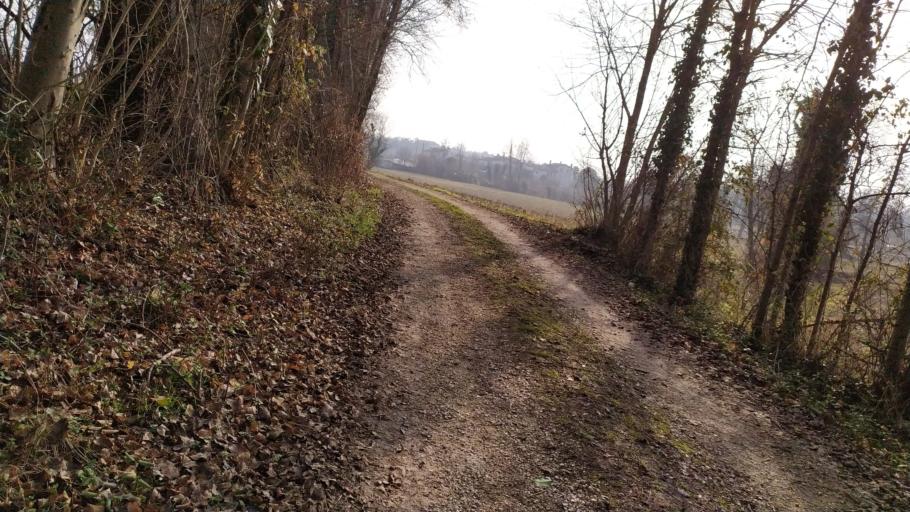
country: IT
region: Veneto
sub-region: Provincia di Treviso
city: Colle Umberto
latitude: 45.9316
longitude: 12.3498
